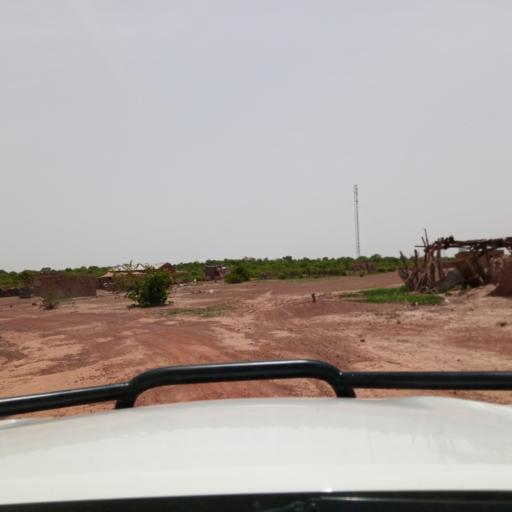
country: ML
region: Koulikoro
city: Koulikoro
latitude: 13.1081
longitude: -7.6100
